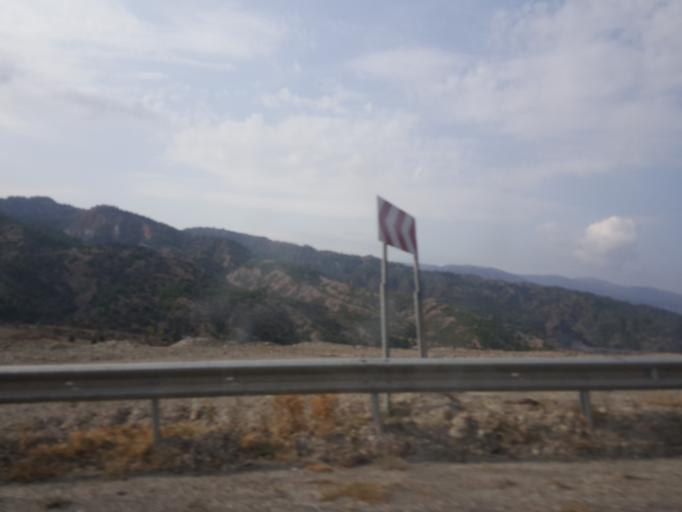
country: TR
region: Corum
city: Kamil
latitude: 41.1072
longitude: 34.7397
